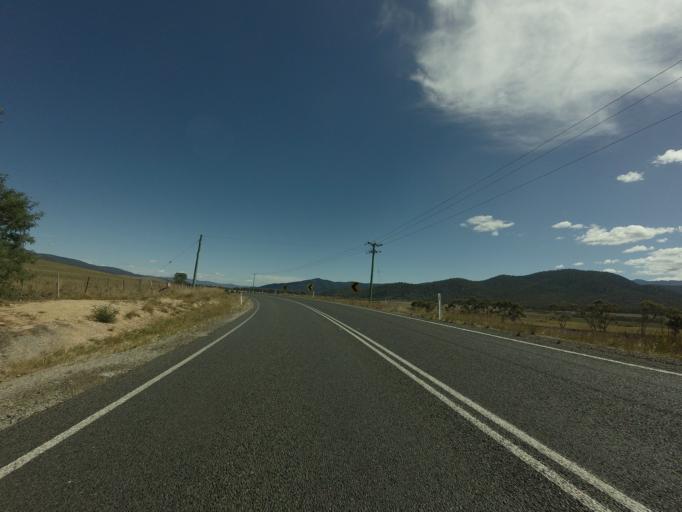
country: AU
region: Tasmania
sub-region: Break O'Day
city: St Helens
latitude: -41.6941
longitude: 147.8652
